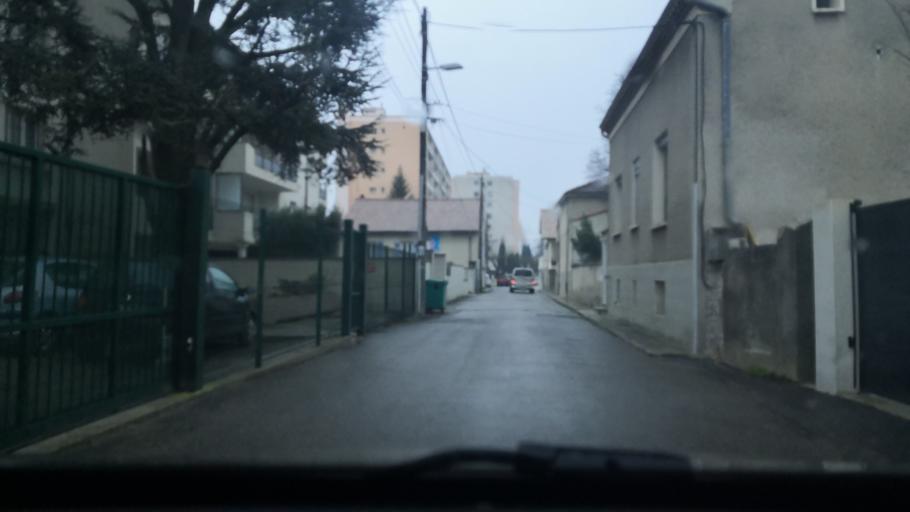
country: FR
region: Rhone-Alpes
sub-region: Departement de la Drome
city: Montelimar
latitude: 44.5557
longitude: 4.7544
